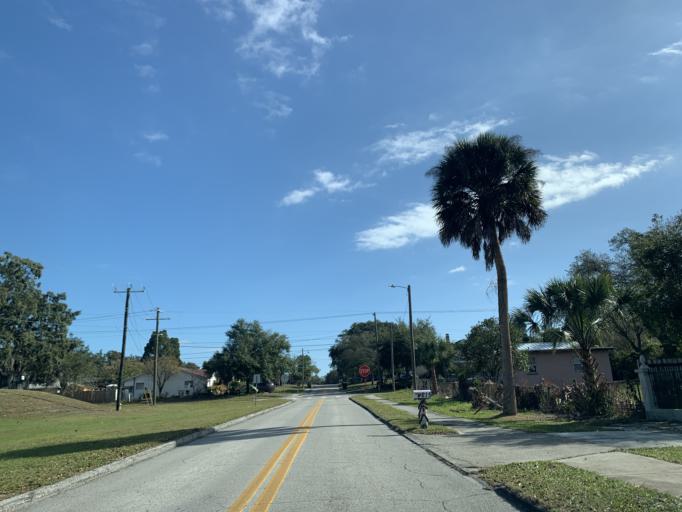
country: US
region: Florida
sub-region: Hillsborough County
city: Temple Terrace
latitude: 28.0398
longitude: -82.4107
